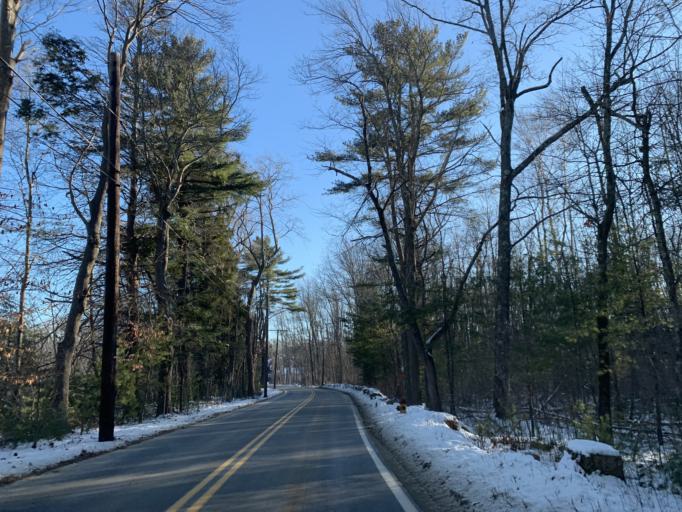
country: US
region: Massachusetts
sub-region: Norfolk County
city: Sharon
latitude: 42.1207
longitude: -71.2072
